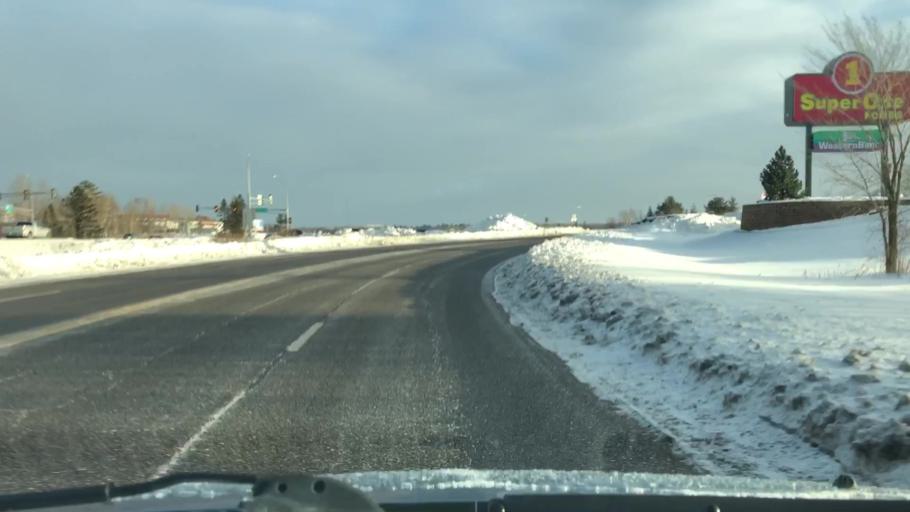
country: US
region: Minnesota
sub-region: Saint Louis County
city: Hermantown
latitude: 46.8114
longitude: -92.1702
